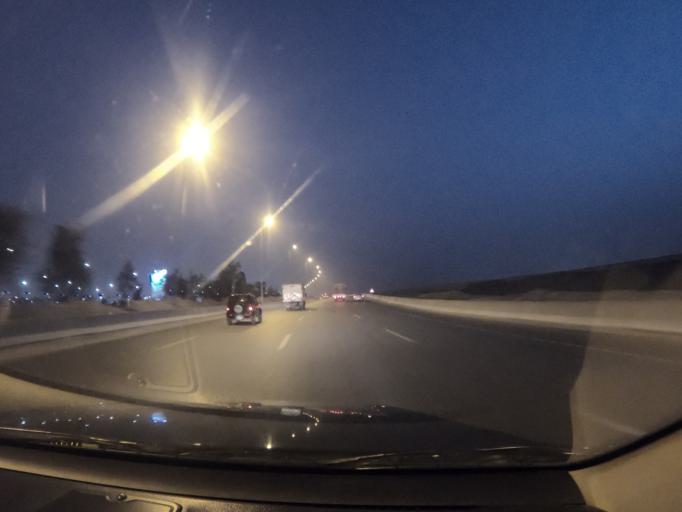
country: EG
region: Muhafazat al Qahirah
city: Cairo
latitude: 30.0292
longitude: 31.4019
